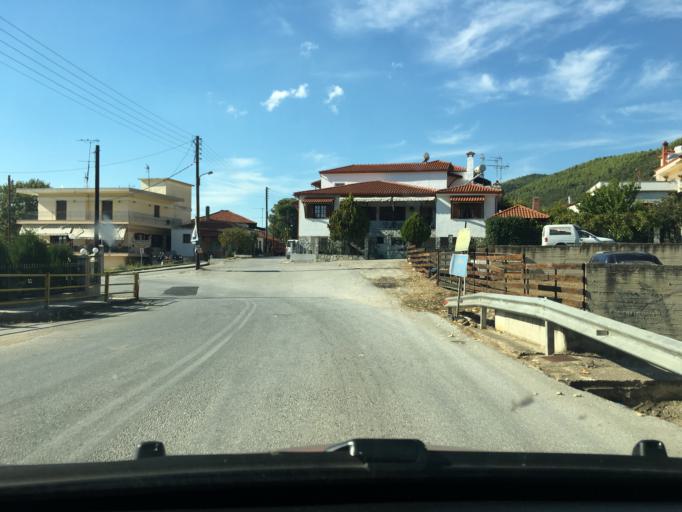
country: GR
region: Central Macedonia
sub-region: Nomos Chalkidikis
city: Ierissos
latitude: 40.3947
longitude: 23.7970
